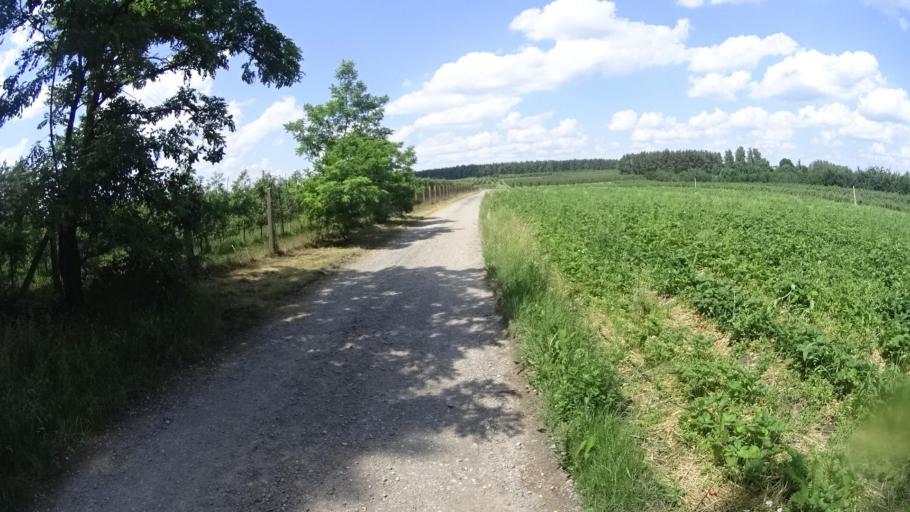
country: PL
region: Masovian Voivodeship
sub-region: Powiat grojecki
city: Goszczyn
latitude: 51.7114
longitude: 20.9071
